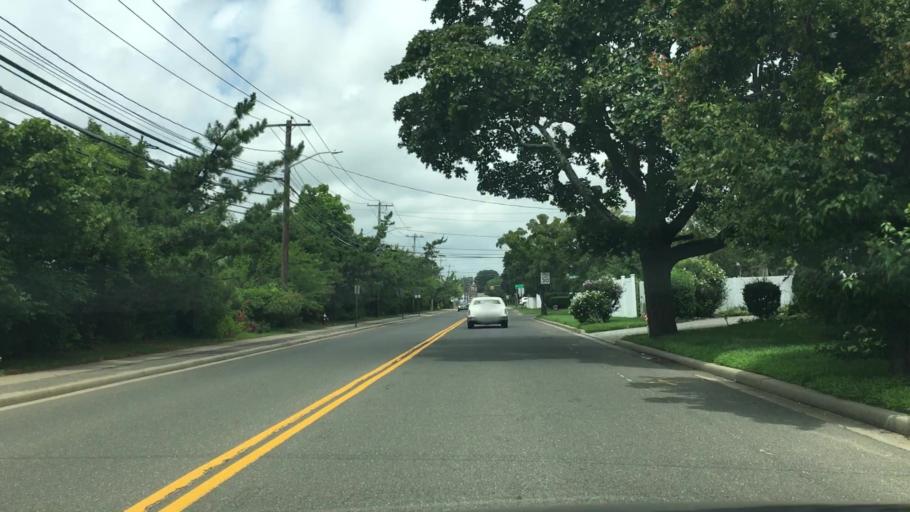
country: US
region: New York
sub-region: Nassau County
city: Hicksville
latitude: 40.7650
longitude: -73.5071
